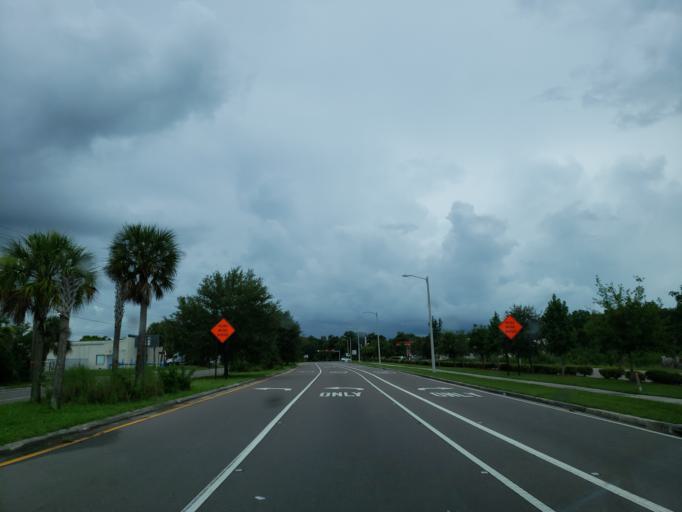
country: US
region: Florida
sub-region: Hillsborough County
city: Ruskin
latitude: 27.7154
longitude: -82.3942
